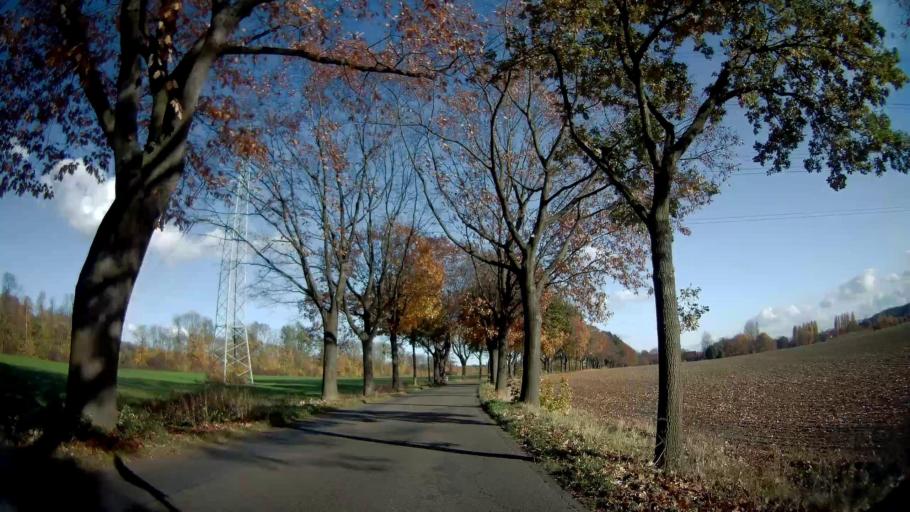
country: DE
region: North Rhine-Westphalia
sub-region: Regierungsbezirk Munster
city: Gladbeck
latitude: 51.5726
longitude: 7.0139
